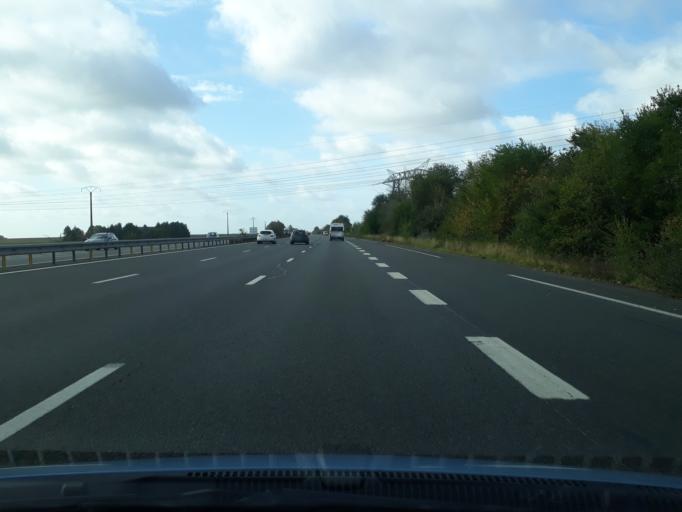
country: FR
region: Centre
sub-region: Departement du Loiret
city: Tavers
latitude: 47.7582
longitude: 1.5524
